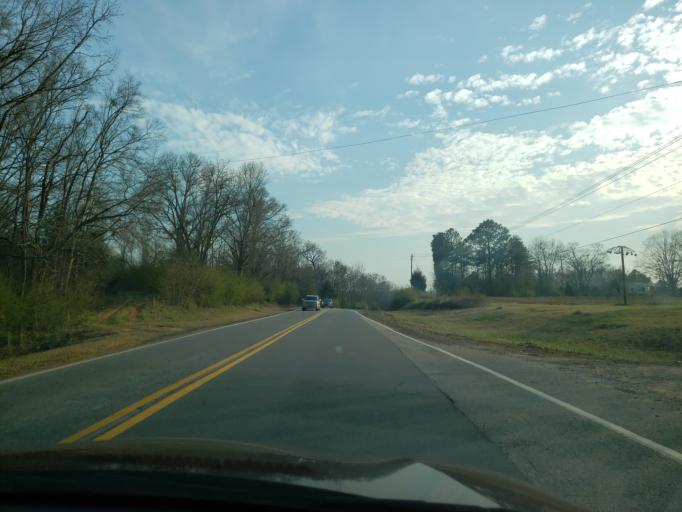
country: US
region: Alabama
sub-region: Hale County
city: Moundville
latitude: 32.9384
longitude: -87.6290
